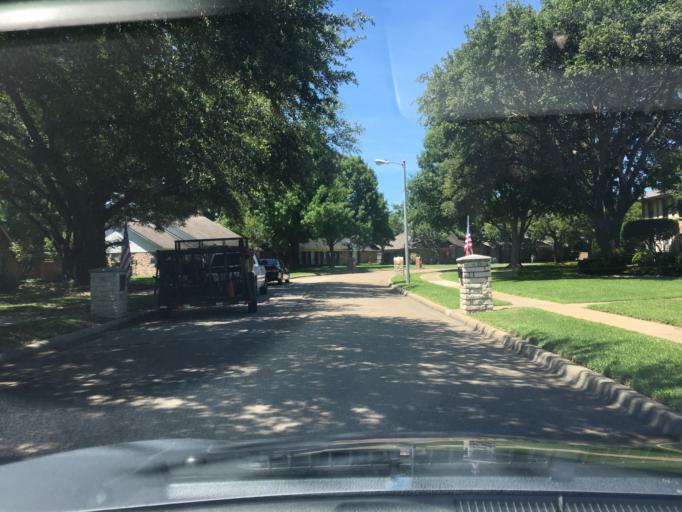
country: US
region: Texas
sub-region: Dallas County
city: Richardson
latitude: 32.9488
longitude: -96.6880
